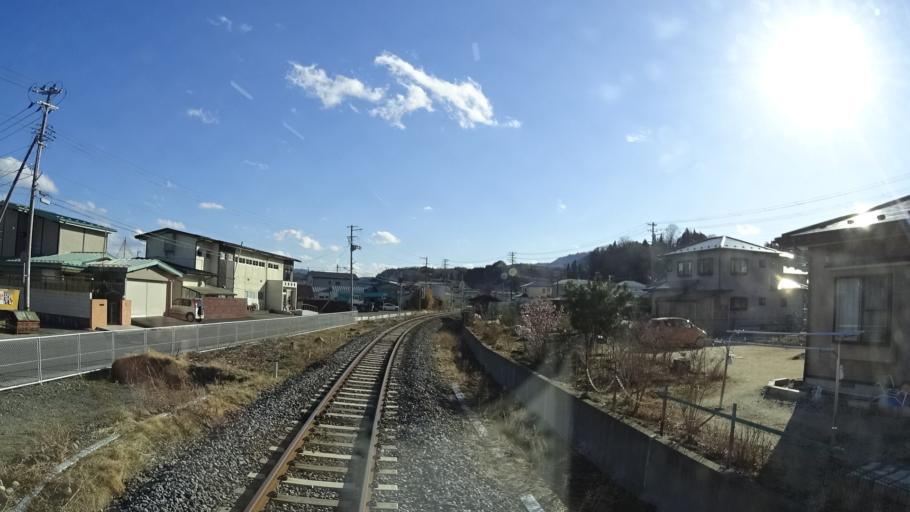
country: JP
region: Iwate
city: Miyako
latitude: 39.5796
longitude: 141.9366
